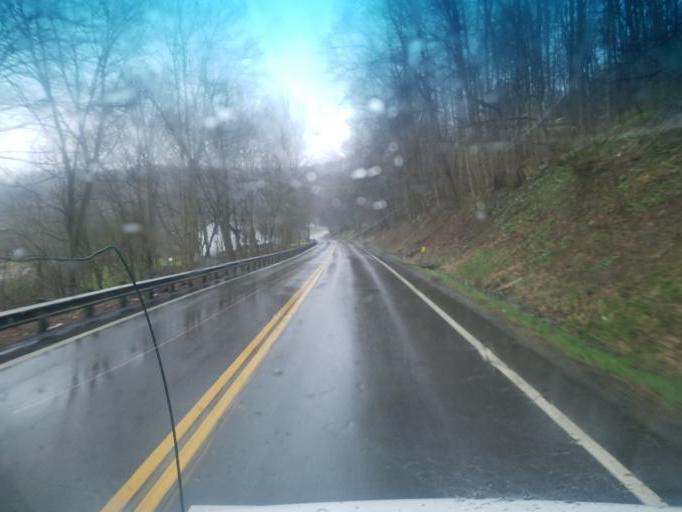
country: US
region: Ohio
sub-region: Holmes County
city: Millersburg
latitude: 40.4997
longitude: -81.9583
